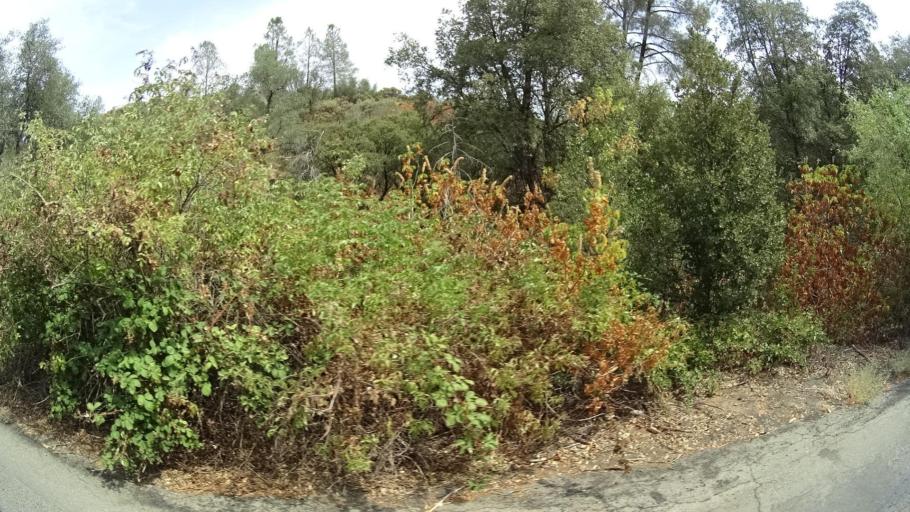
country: US
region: California
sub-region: Mariposa County
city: Midpines
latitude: 37.5651
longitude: -119.9580
